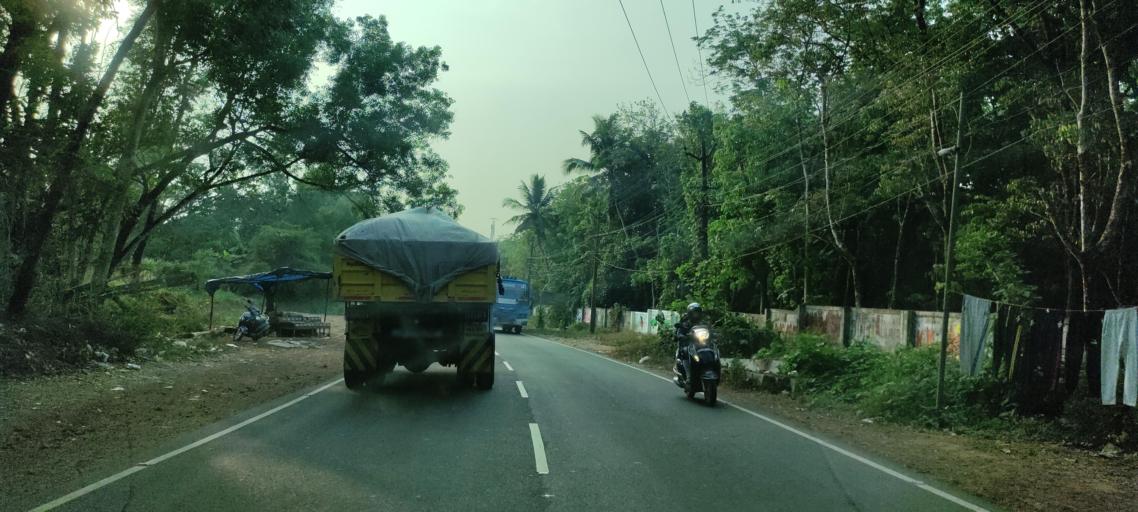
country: IN
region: Kerala
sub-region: Alappuzha
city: Kattanam
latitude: 9.1752
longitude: 76.6224
